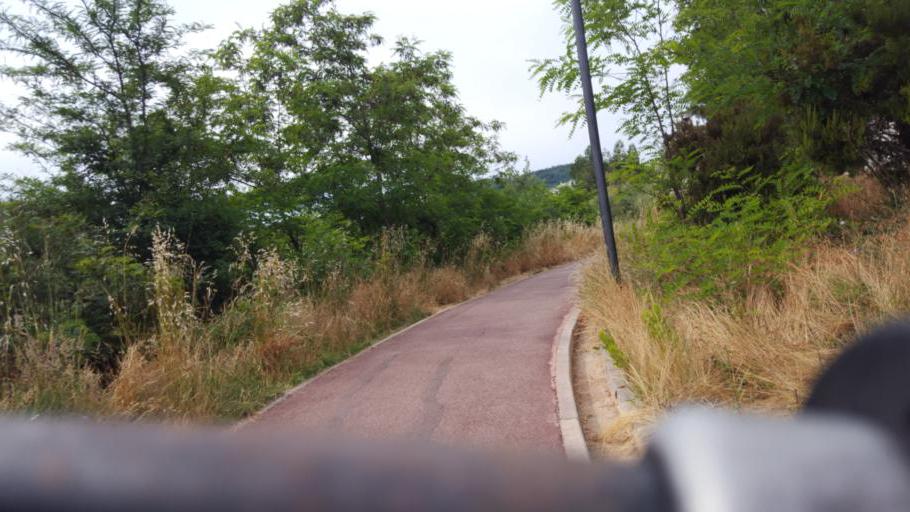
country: AL
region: Tirane
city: Tirana
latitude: 41.3092
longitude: 19.8152
